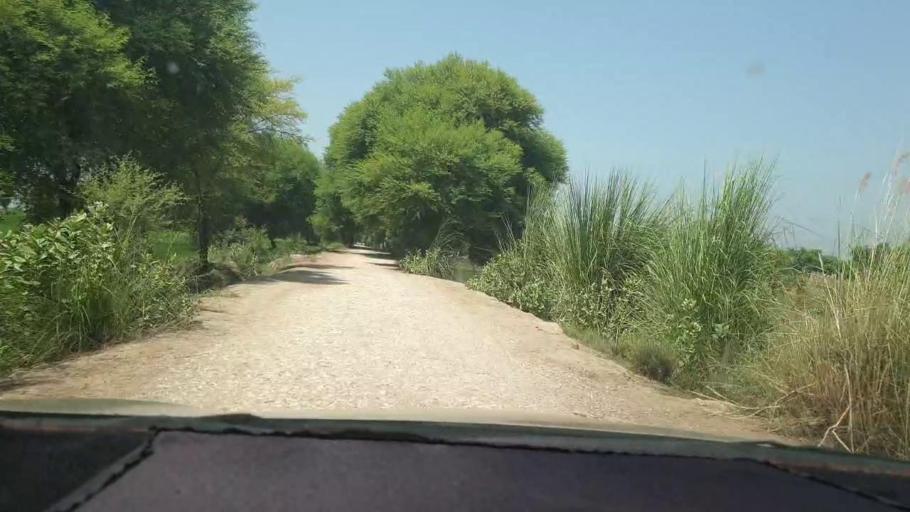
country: PK
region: Sindh
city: Kambar
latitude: 27.6075
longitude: 68.0850
